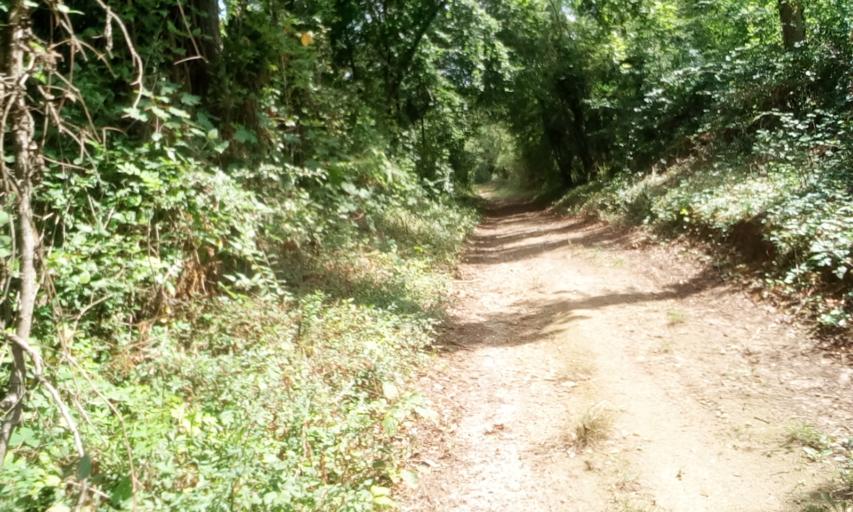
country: FR
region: Lower Normandy
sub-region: Departement du Calvados
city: Cagny
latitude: 49.1134
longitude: -0.2532
